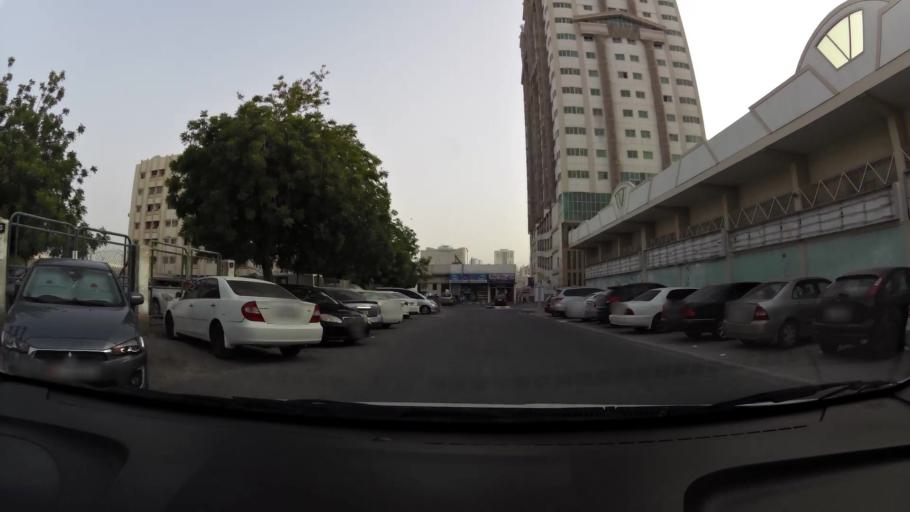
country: AE
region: Ash Shariqah
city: Sharjah
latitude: 25.3417
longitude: 55.4018
